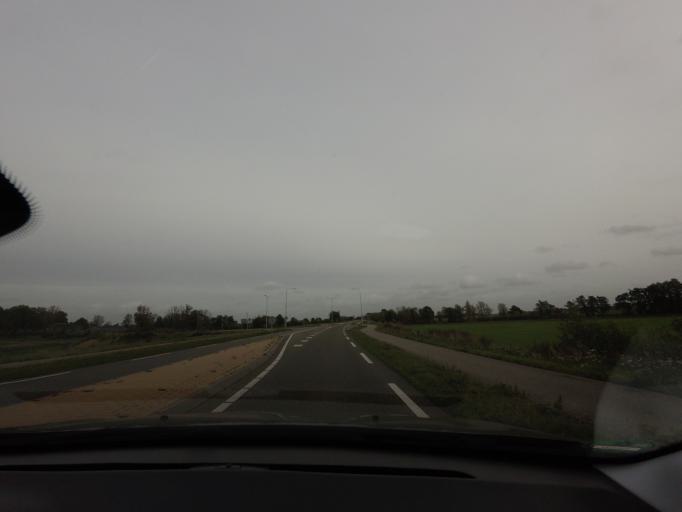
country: NL
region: Overijssel
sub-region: Gemeente Steenwijkerland
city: Blokzijl
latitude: 52.7442
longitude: 5.9924
